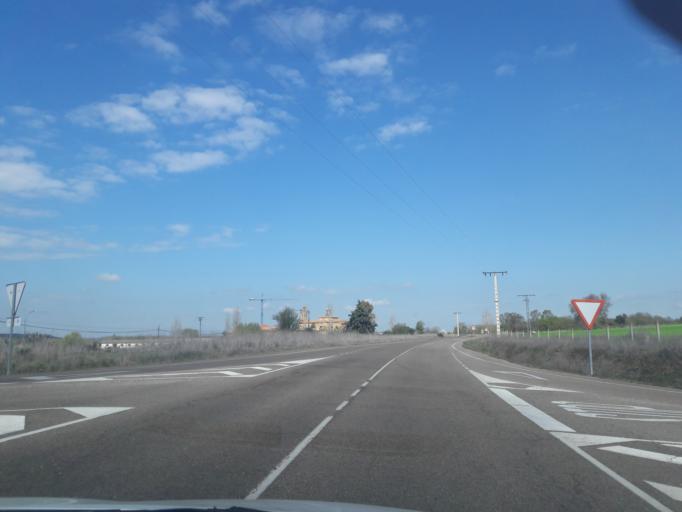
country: ES
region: Castille and Leon
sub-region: Provincia de Salamanca
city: Ciudad Rodrigo
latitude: 40.5714
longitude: -6.4899
